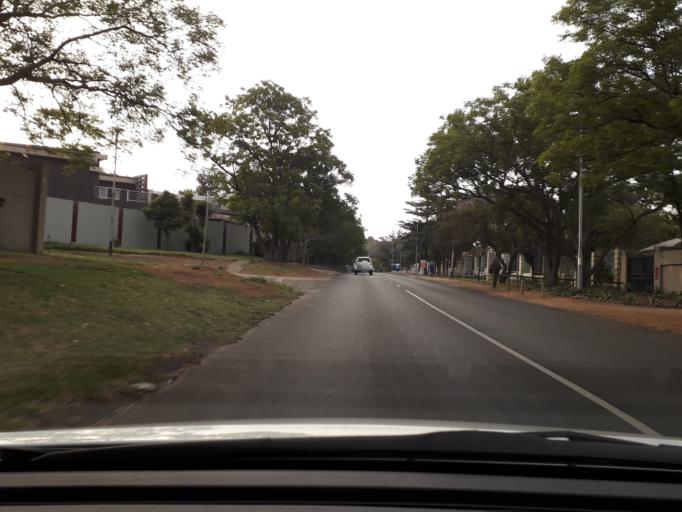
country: ZA
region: Gauteng
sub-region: City of Johannesburg Metropolitan Municipality
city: Midrand
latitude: -26.0528
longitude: 28.0396
